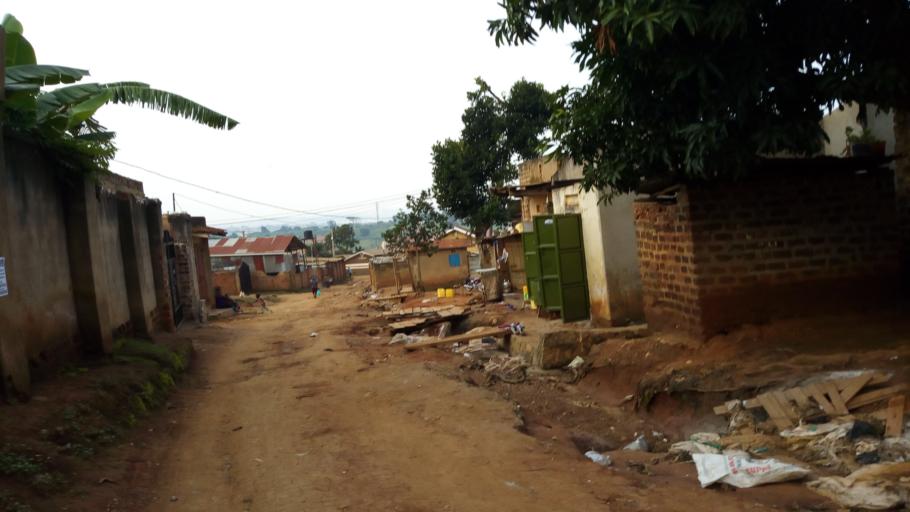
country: UG
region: Central Region
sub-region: Wakiso District
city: Kireka
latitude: 0.3131
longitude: 32.6490
